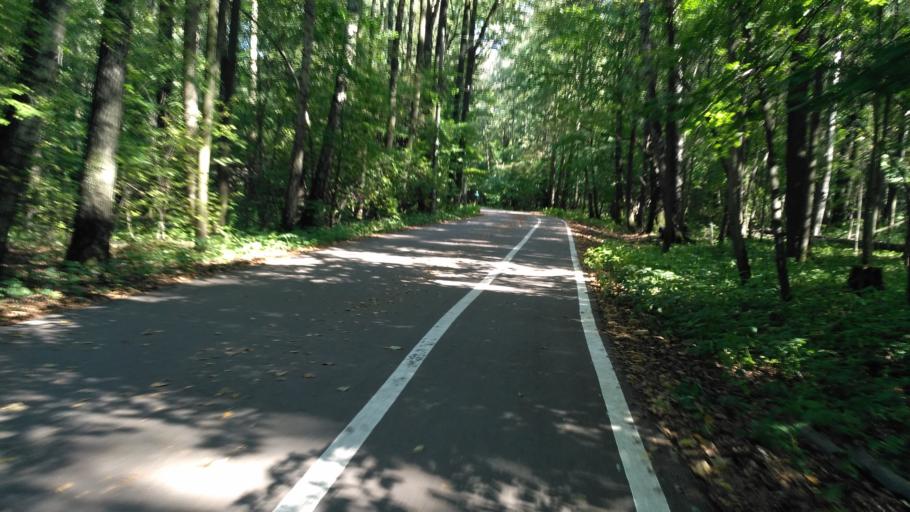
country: RU
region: Moskovskaya
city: Izmaylovo
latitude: 55.7761
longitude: 37.7695
